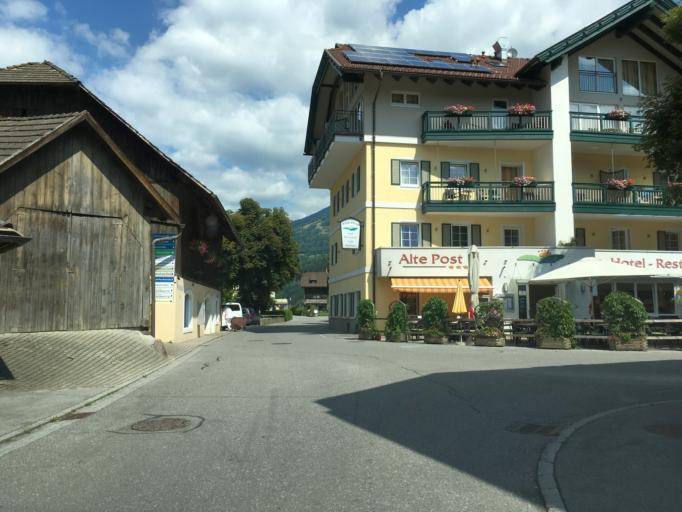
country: AT
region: Carinthia
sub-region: Politischer Bezirk Villach Land
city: Feld am See
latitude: 46.7756
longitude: 13.7461
